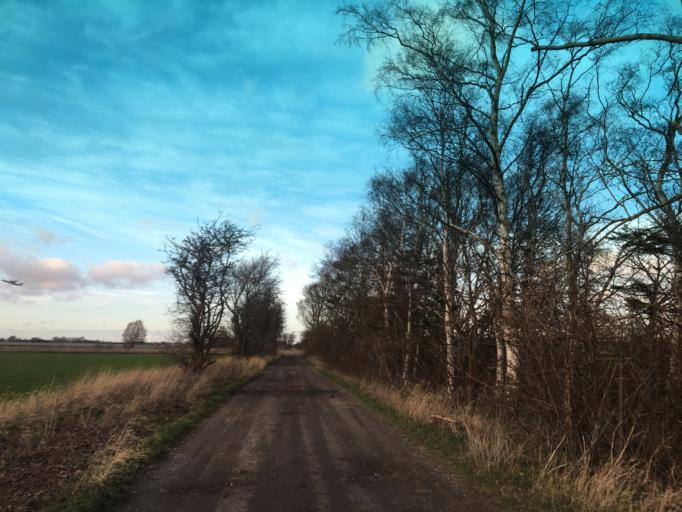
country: DK
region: Capital Region
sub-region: Tarnby Kommune
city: Tarnby
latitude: 55.5937
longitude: 12.6209
